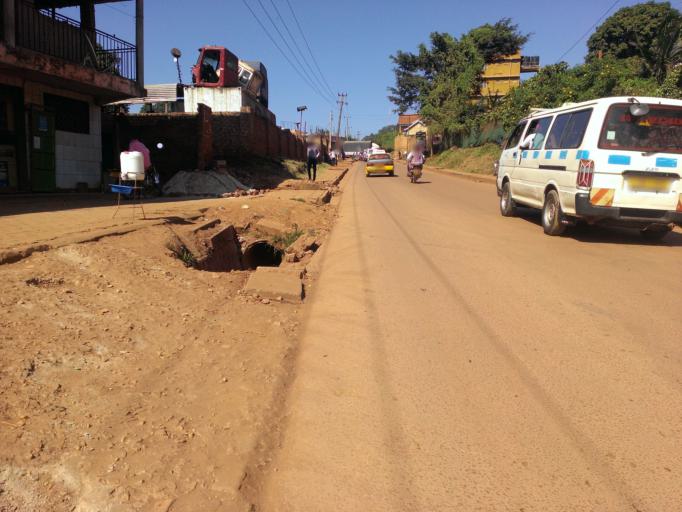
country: UG
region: Central Region
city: Kampala Central Division
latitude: 0.3226
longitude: 32.5644
